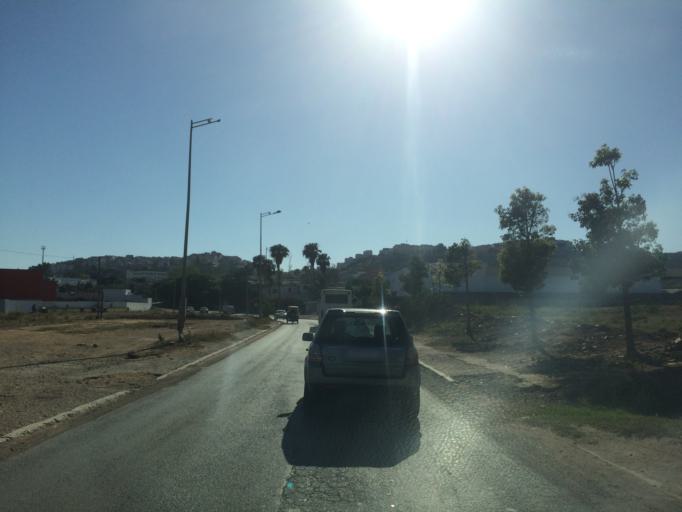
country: MA
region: Rabat-Sale-Zemmour-Zaer
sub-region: Rabat
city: Rabat
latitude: 33.9912
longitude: -6.8011
